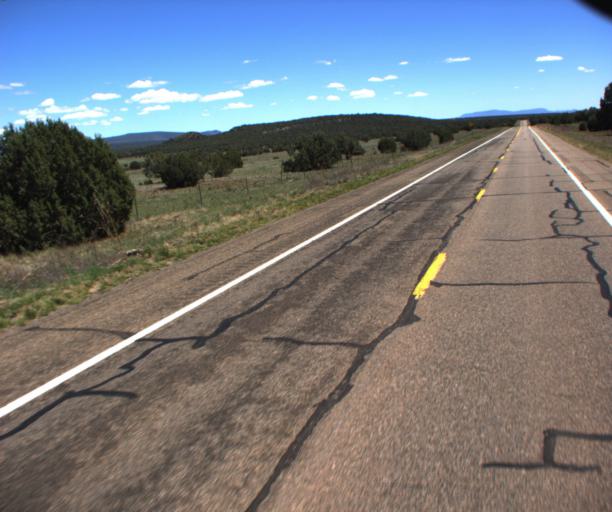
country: US
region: Arizona
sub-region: Yavapai County
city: Paulden
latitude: 35.1484
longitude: -112.4485
